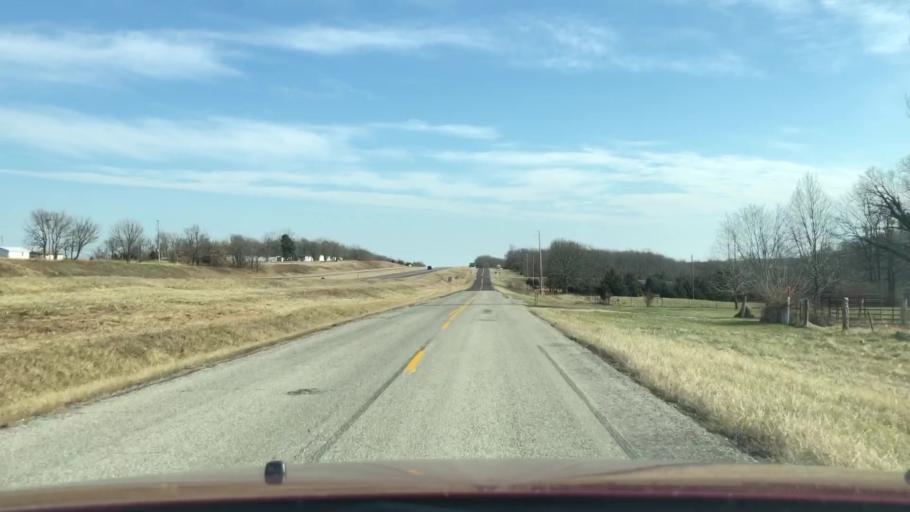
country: US
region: Missouri
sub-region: Wright County
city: Mansfield
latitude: 37.1119
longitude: -92.6335
